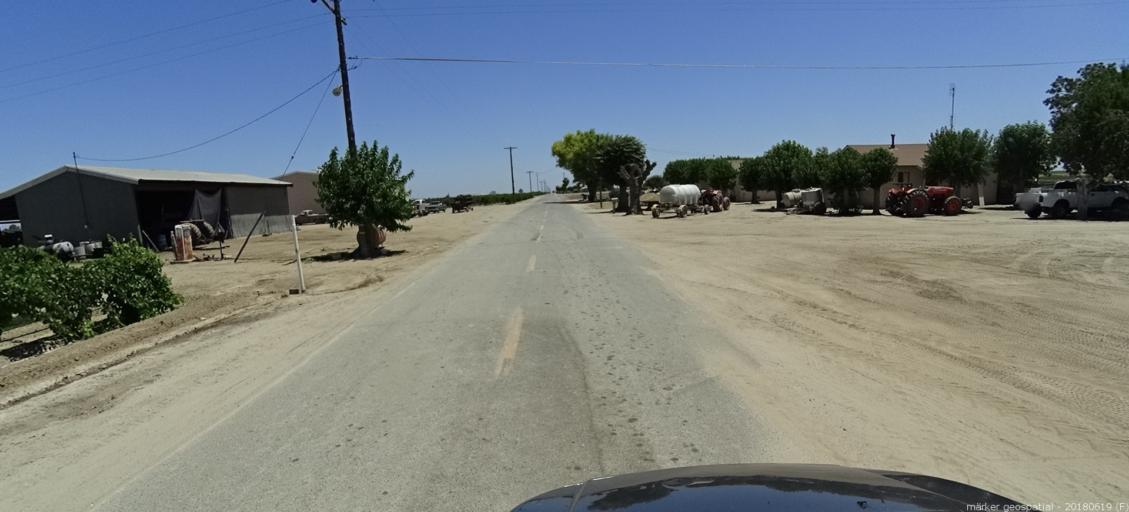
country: US
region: California
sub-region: Madera County
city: Parkwood
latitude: 36.8585
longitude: -120.1445
